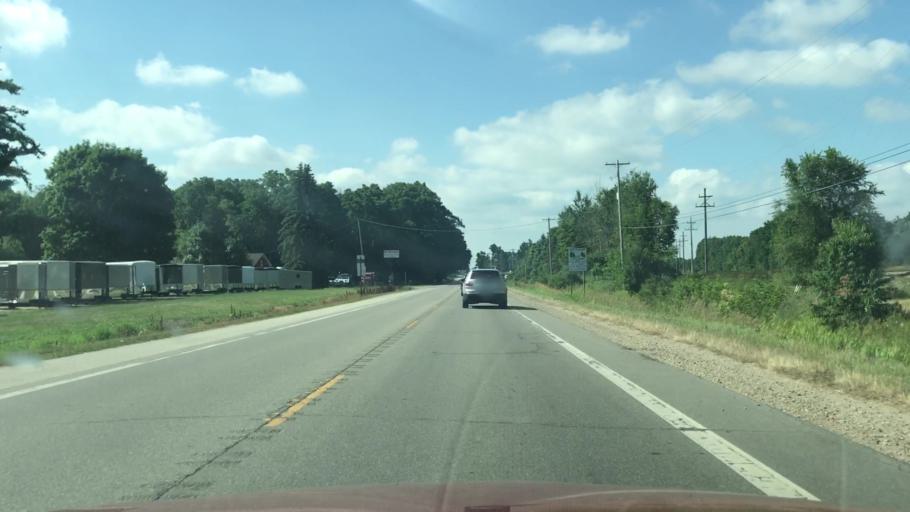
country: US
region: Michigan
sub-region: Newaygo County
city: Newaygo
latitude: 43.3212
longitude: -85.8106
